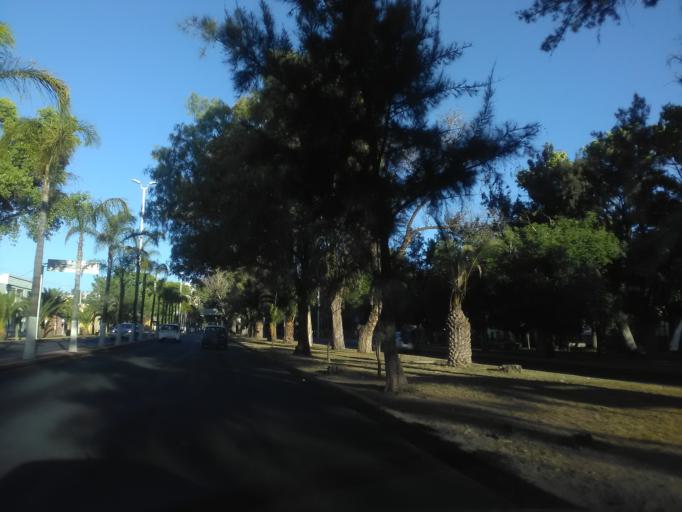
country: MX
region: Durango
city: Victoria de Durango
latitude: 24.0202
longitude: -104.6697
